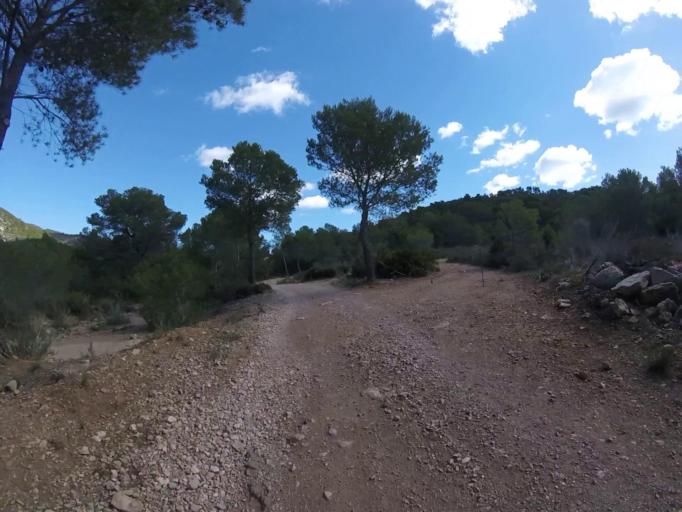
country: ES
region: Valencia
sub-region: Provincia de Castello
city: Alcoceber
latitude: 40.2930
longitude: 0.3142
